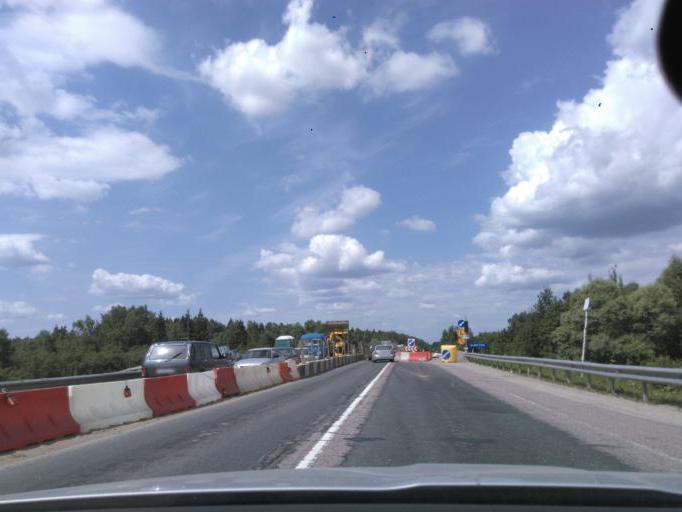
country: RU
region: Moskovskaya
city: Solnechnogorsk
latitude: 56.1437
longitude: 36.9510
